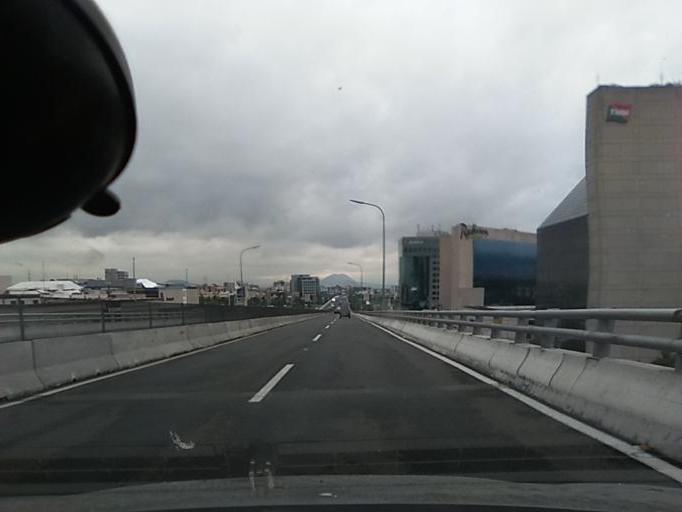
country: MX
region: Mexico City
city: Tlalpan
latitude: 19.3021
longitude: -99.1922
